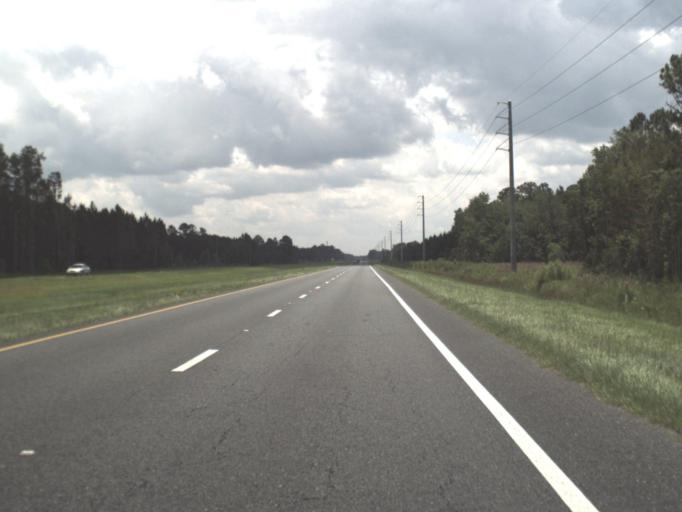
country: US
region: Florida
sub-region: Levy County
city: Bronson
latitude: 29.4739
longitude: -82.6795
